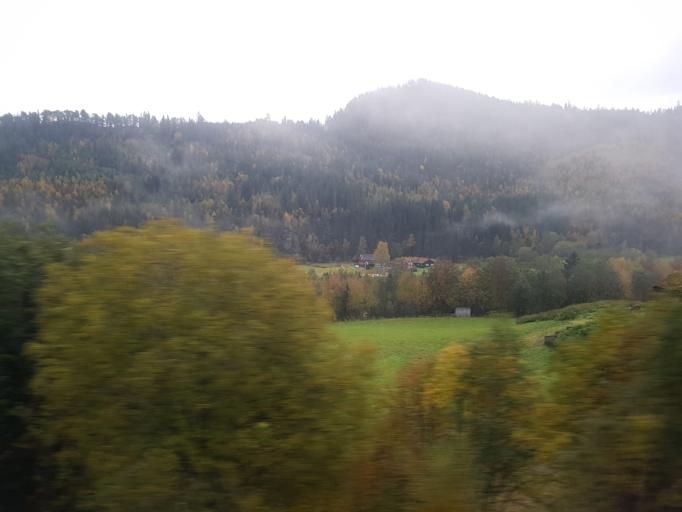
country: NO
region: Sor-Trondelag
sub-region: Midtre Gauldal
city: Storen
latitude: 63.0306
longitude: 10.2684
